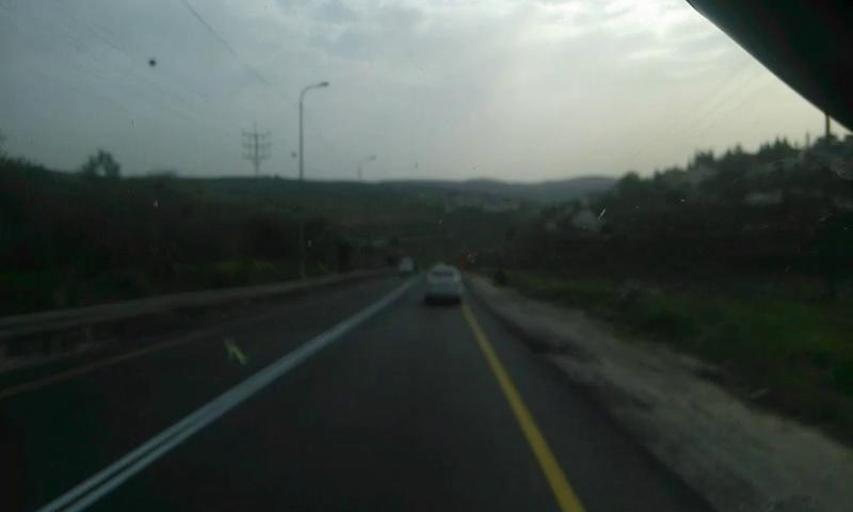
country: PS
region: West Bank
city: Jit
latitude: 32.2133
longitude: 35.1659
